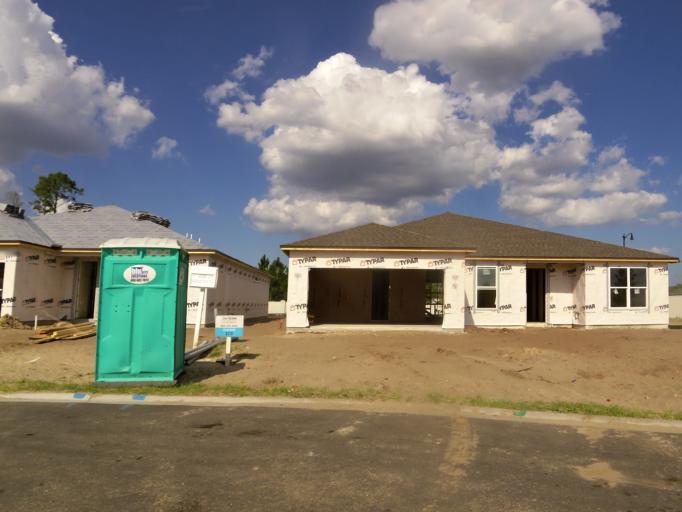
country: US
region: Florida
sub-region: Saint Johns County
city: Palm Valley
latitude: 30.1755
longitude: -81.5068
